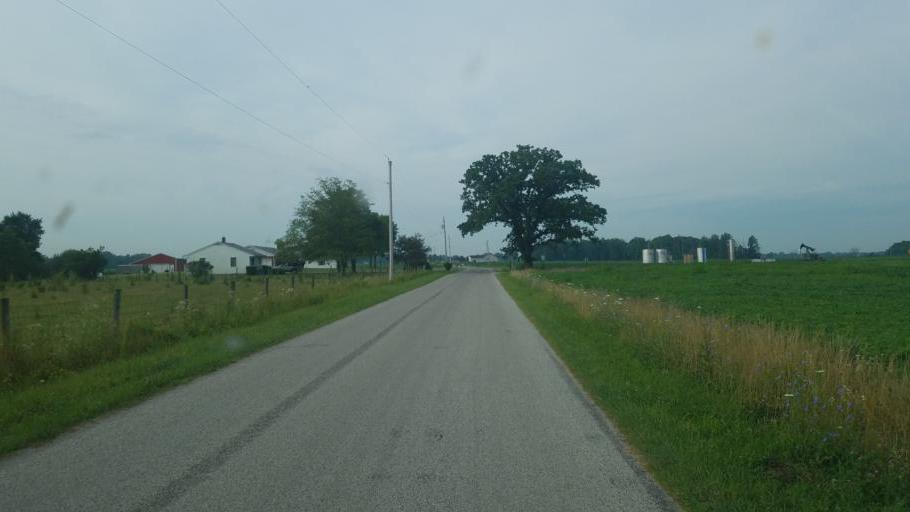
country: US
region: Ohio
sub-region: Morrow County
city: Cardington
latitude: 40.5286
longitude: -82.8771
